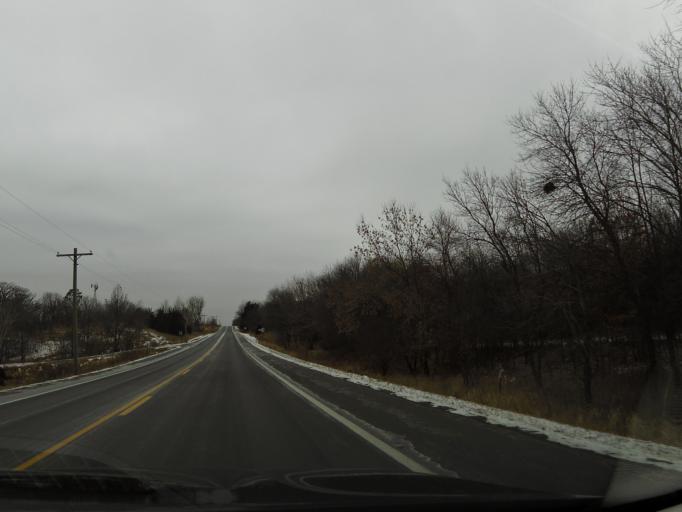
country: US
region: Minnesota
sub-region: Hennepin County
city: Medina
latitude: 45.0223
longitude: -93.6080
